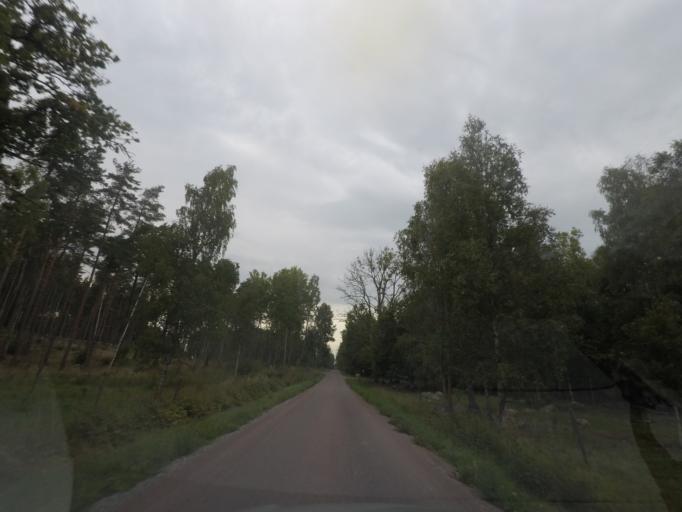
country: SE
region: Vaestmanland
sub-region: Hallstahammars Kommun
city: Kolback
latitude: 59.4926
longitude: 16.1925
